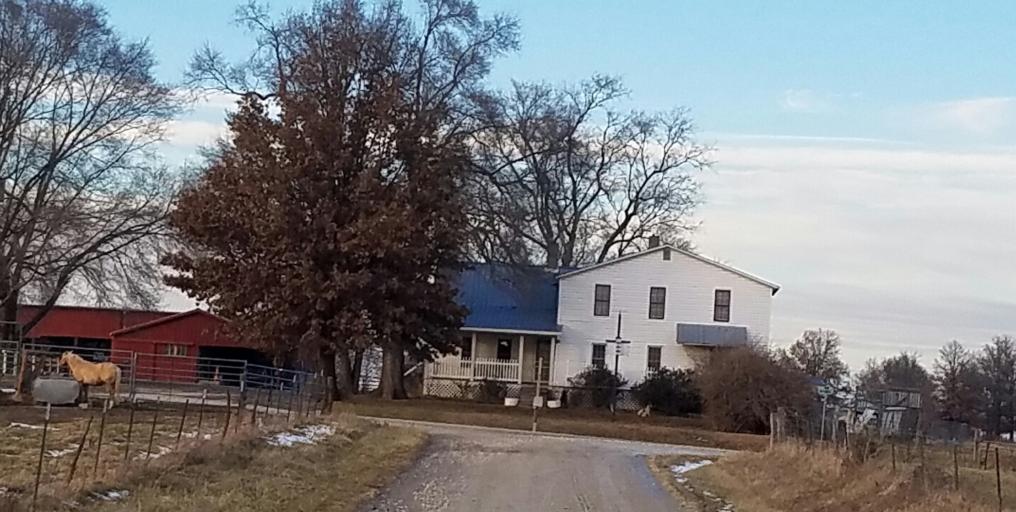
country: US
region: Missouri
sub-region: Randolph County
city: Moberly
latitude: 39.3333
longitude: -92.3031
